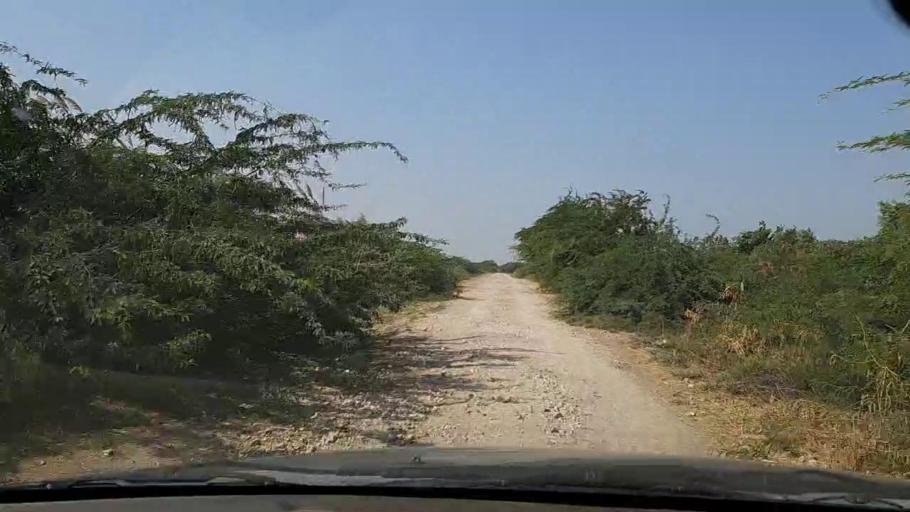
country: PK
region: Sindh
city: Chuhar Jamali
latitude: 24.4406
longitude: 67.7995
